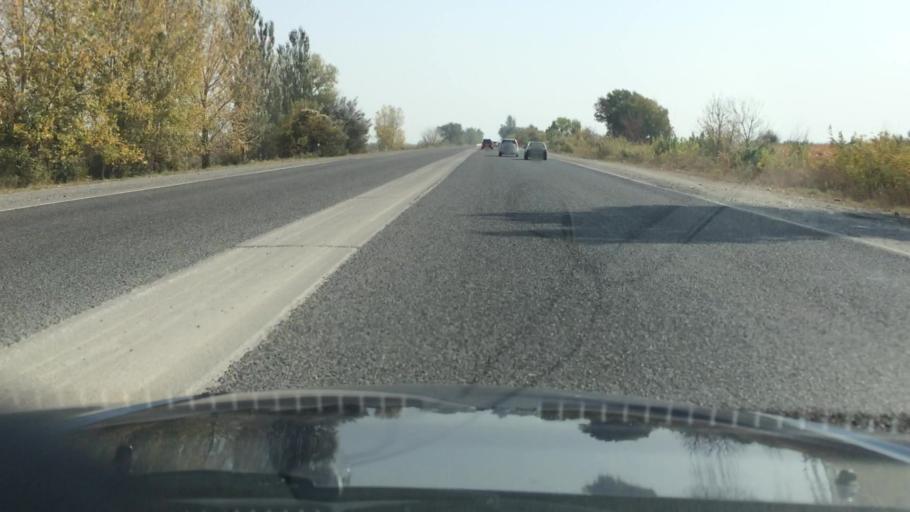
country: KG
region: Chuy
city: Kant
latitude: 42.9564
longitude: 74.9339
